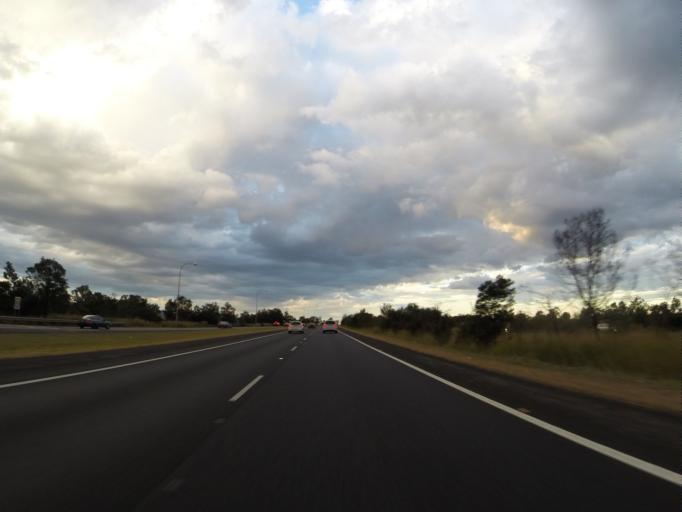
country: AU
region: New South Wales
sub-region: Wollondilly
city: Douglas Park
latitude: -34.2268
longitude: 150.6698
